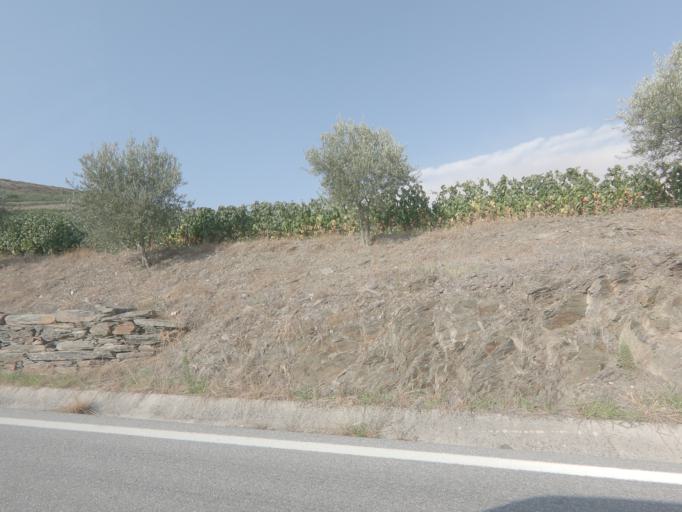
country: PT
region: Viseu
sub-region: Tabuaco
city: Tabuaco
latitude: 41.1397
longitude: -7.5415
